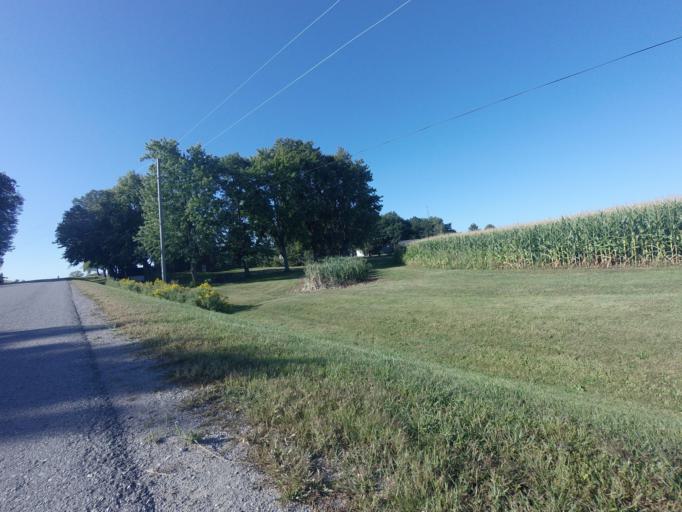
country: CA
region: Ontario
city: Bradford West Gwillimbury
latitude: 44.0496
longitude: -79.6267
